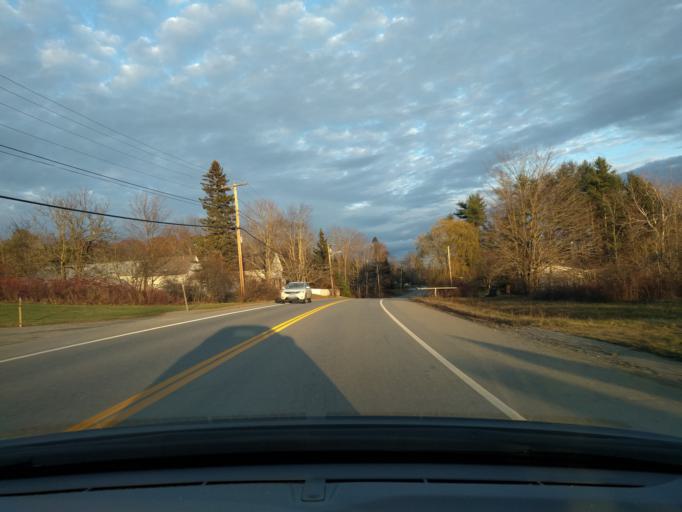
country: US
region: Maine
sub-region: Waldo County
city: Winterport
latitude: 44.6299
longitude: -68.8623
